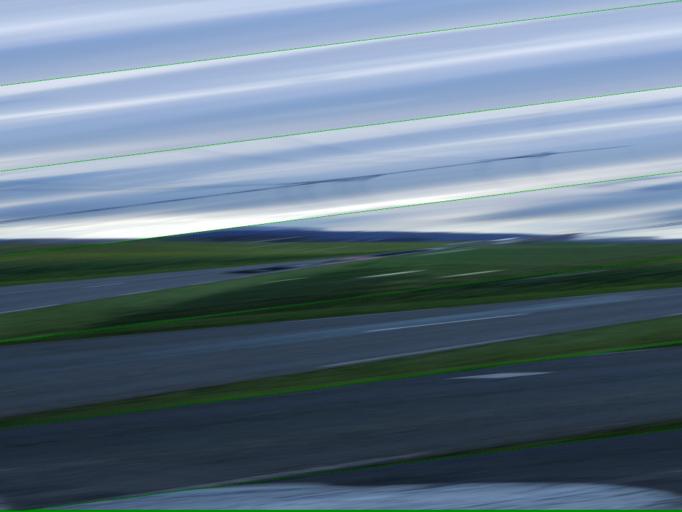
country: FR
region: Picardie
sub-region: Departement de l'Oise
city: Chaumont-en-Vexin
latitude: 49.3210
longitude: 1.8918
